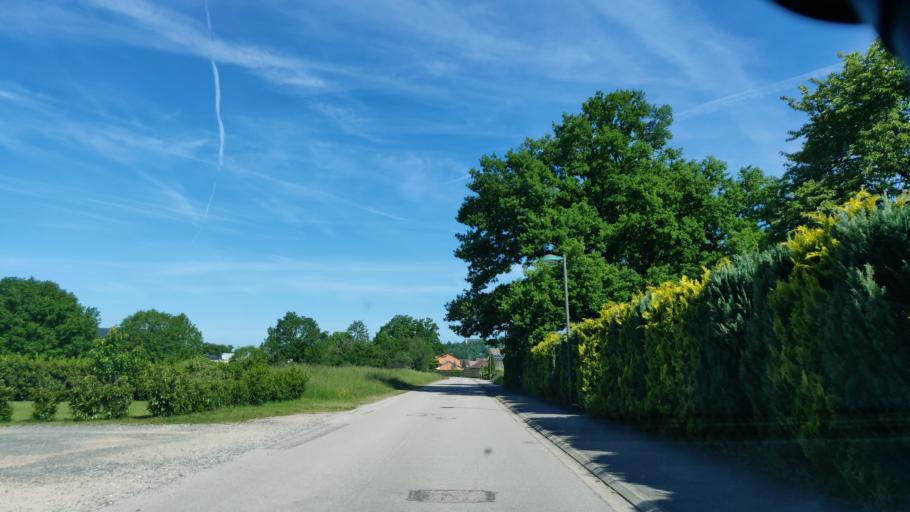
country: FR
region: Lorraine
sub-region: Departement des Vosges
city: Sainte-Marguerite
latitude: 48.2738
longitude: 6.9781
